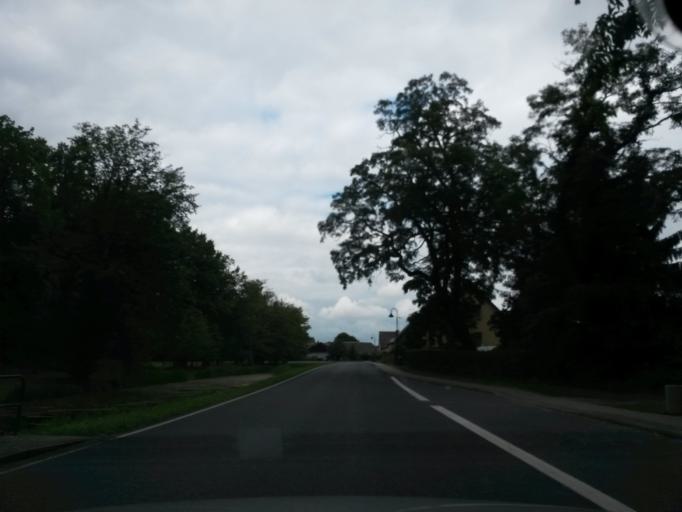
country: DE
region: Brandenburg
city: Gerswalde
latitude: 53.1578
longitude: 13.8479
